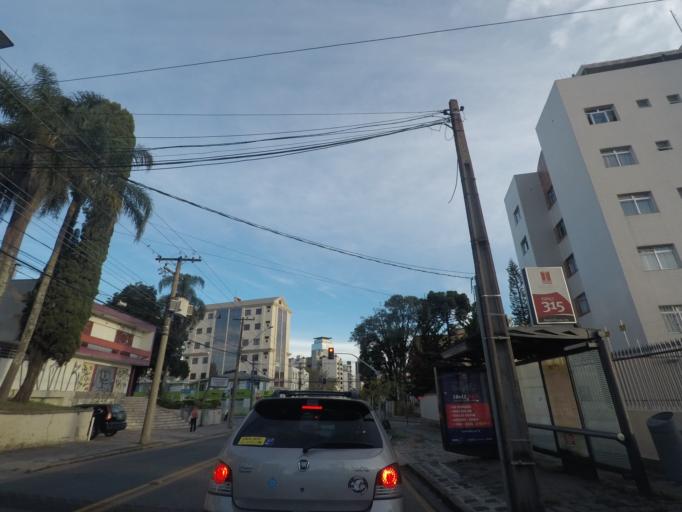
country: BR
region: Parana
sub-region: Curitiba
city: Curitiba
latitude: -25.4124
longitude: -49.2637
